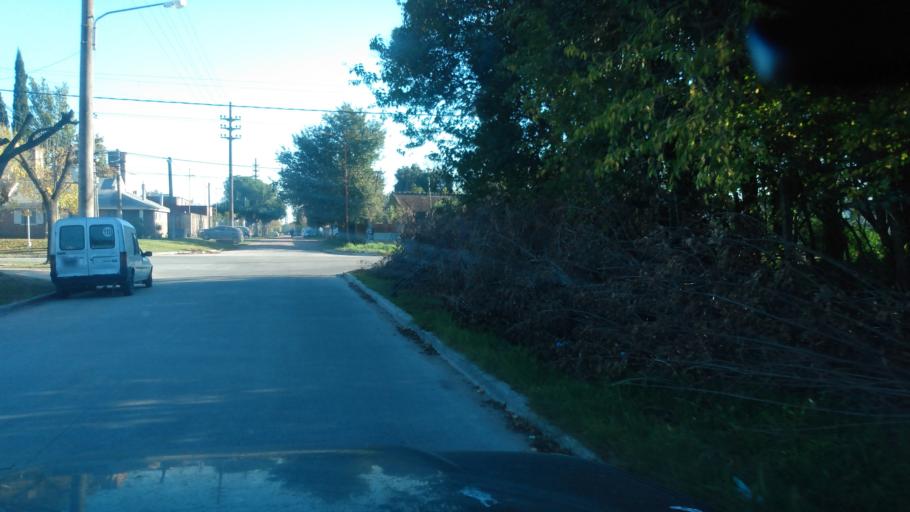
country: AR
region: Buenos Aires
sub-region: Partido de Lujan
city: Lujan
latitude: -34.5579
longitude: -59.1025
